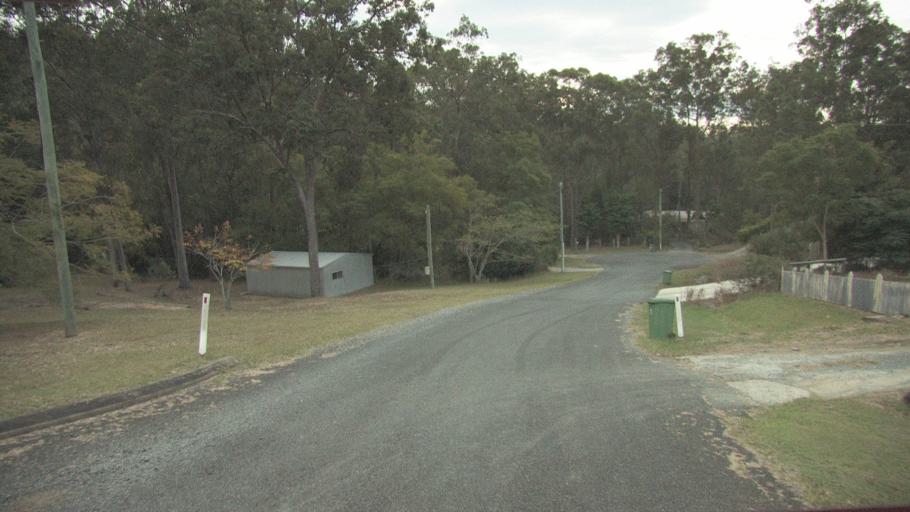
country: AU
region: Queensland
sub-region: Logan
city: Chambers Flat
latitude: -27.8246
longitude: 153.0920
